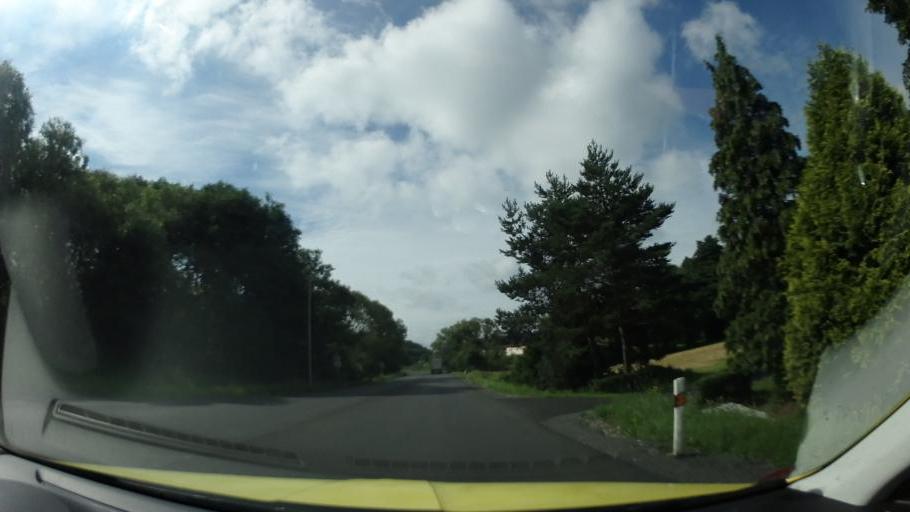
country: CZ
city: Hodslavice
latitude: 49.5646
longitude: 18.0255
